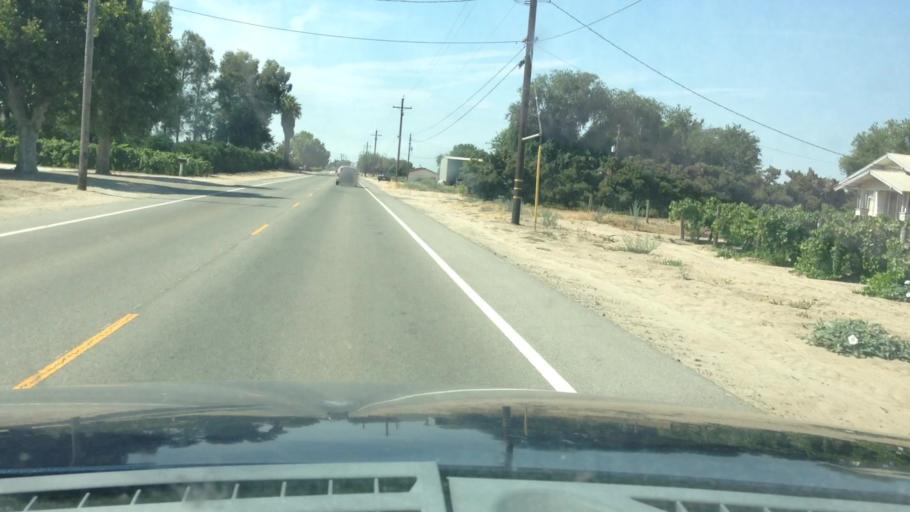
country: US
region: California
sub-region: Fresno County
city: Kingsburg
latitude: 36.5532
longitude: -119.5566
